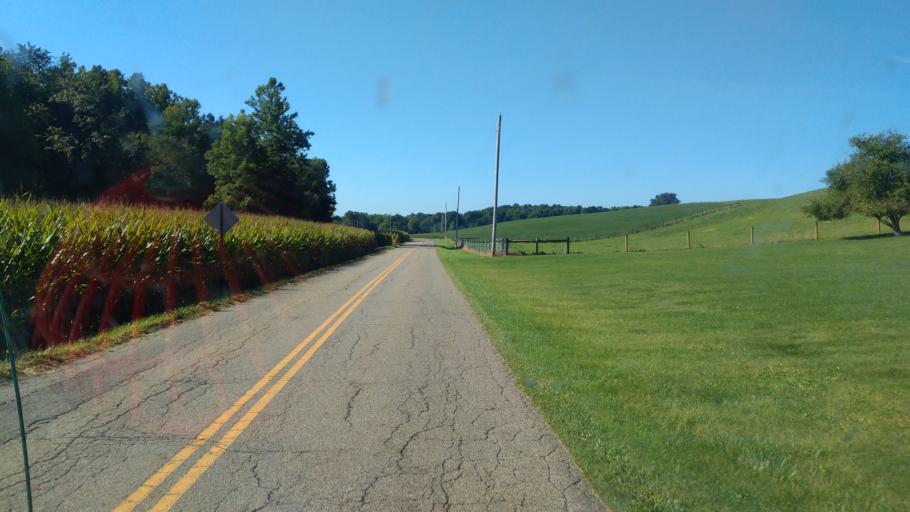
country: US
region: Ohio
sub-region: Knox County
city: Gambier
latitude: 40.4506
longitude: -82.3769
